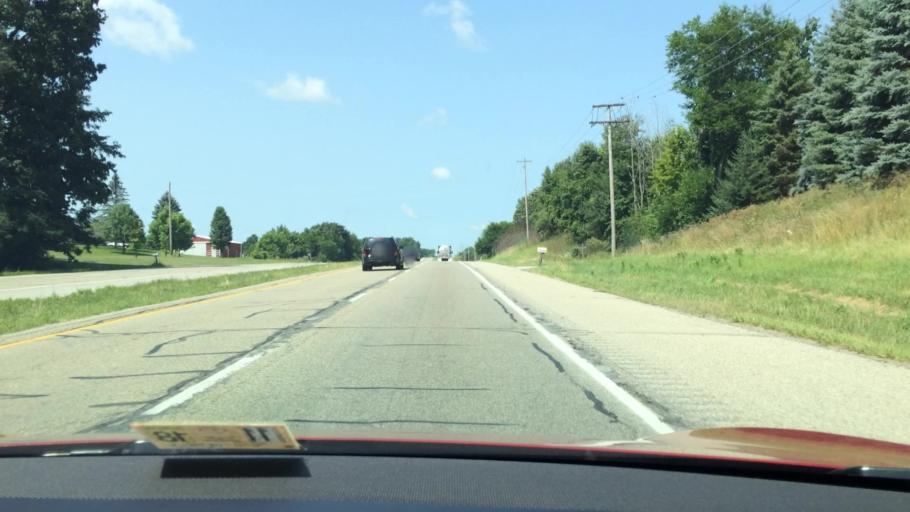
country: US
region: Indiana
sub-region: LaPorte County
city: Hudson Lake
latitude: 41.6726
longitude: -86.5457
